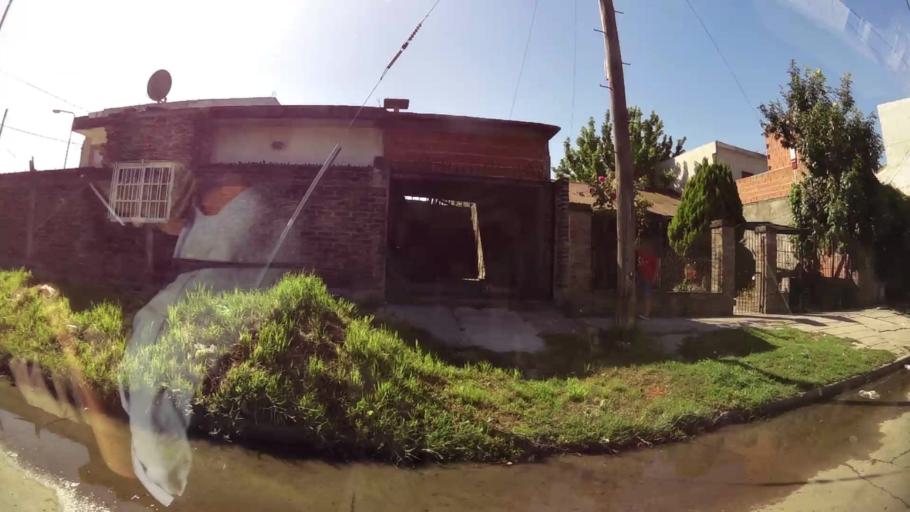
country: AR
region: Buenos Aires
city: Hurlingham
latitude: -34.5389
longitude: -58.5933
